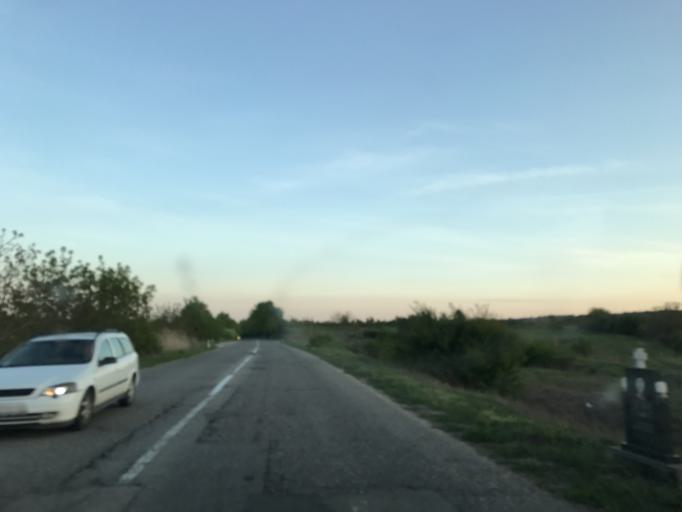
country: RS
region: Central Serbia
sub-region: Borski Okrug
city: Negotin
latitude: 44.2821
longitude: 22.5064
